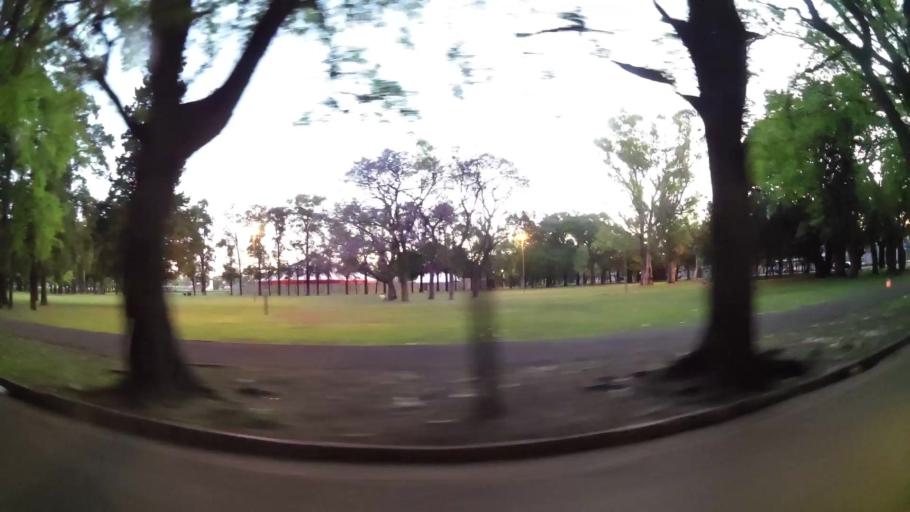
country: AR
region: Santa Fe
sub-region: Departamento de Rosario
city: Rosario
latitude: -32.9555
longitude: -60.6638
